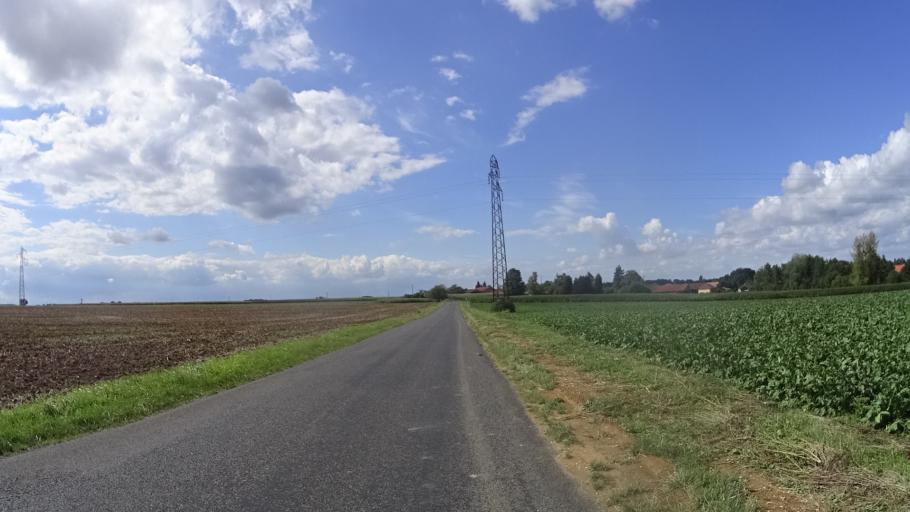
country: FR
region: Champagne-Ardenne
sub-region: Departement de la Marne
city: Pargny-sur-Saulx
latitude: 48.7131
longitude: 4.7845
